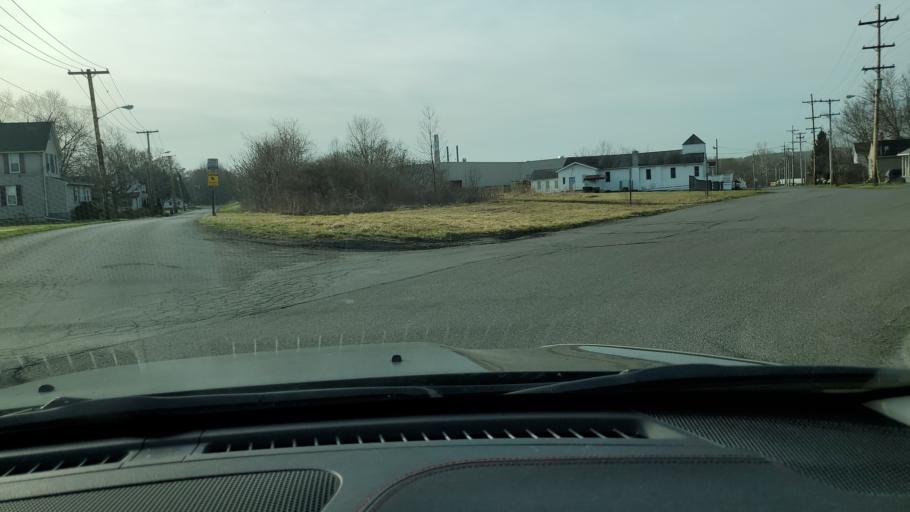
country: US
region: Ohio
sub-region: Trumbull County
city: Niles
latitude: 41.1787
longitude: -80.7545
